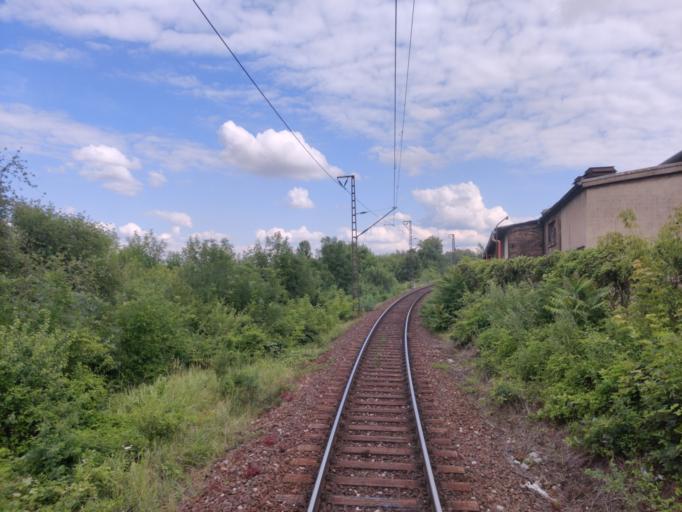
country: DE
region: Saxony-Anhalt
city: Blankenburg
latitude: 51.7998
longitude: 10.9411
